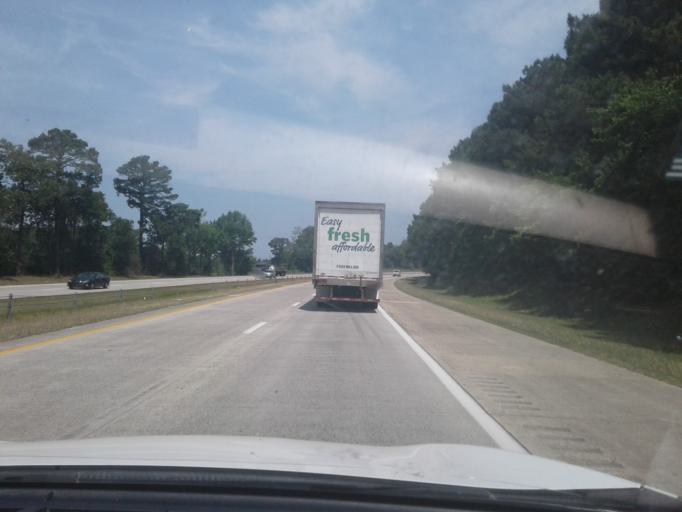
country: US
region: North Carolina
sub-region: Johnston County
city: Clayton
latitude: 35.5447
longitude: -78.5785
